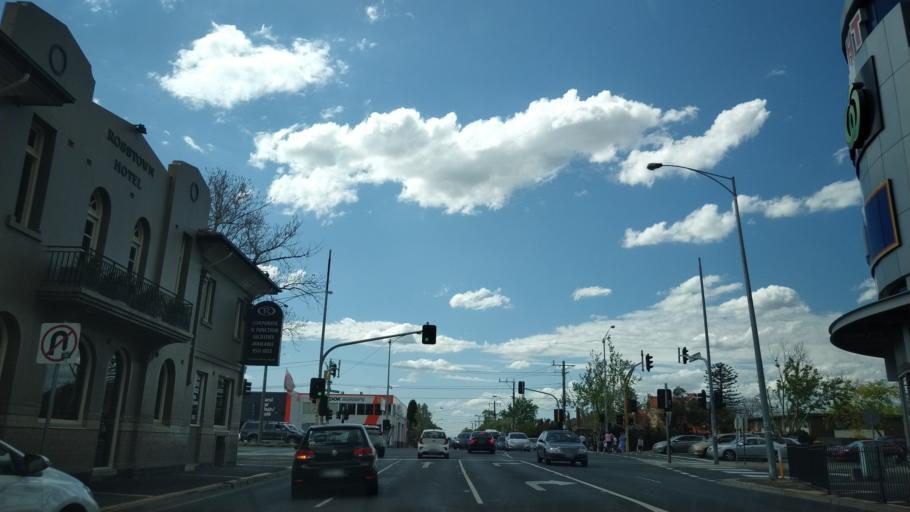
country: AU
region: Victoria
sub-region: Glen Eira
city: Carnegie
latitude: -37.8845
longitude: 145.0579
